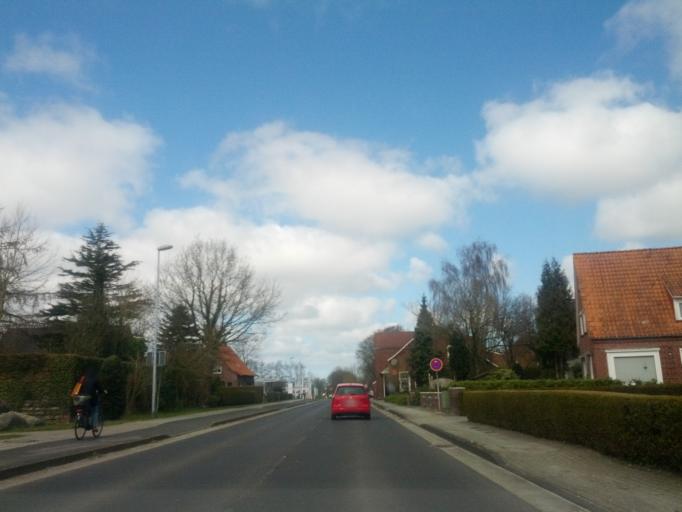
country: DE
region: Lower Saxony
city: Esens
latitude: 53.6515
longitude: 7.6114
